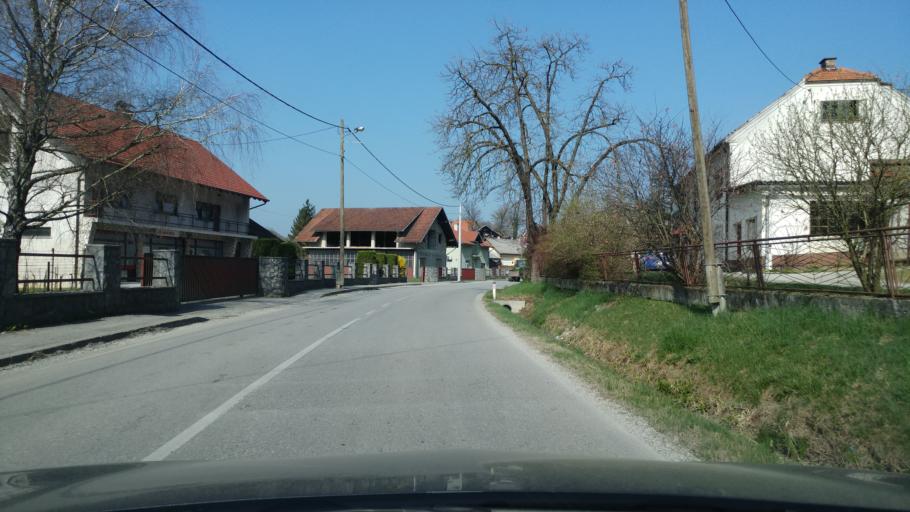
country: HR
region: Zagrebacka
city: Pojatno
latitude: 45.9182
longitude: 15.7737
